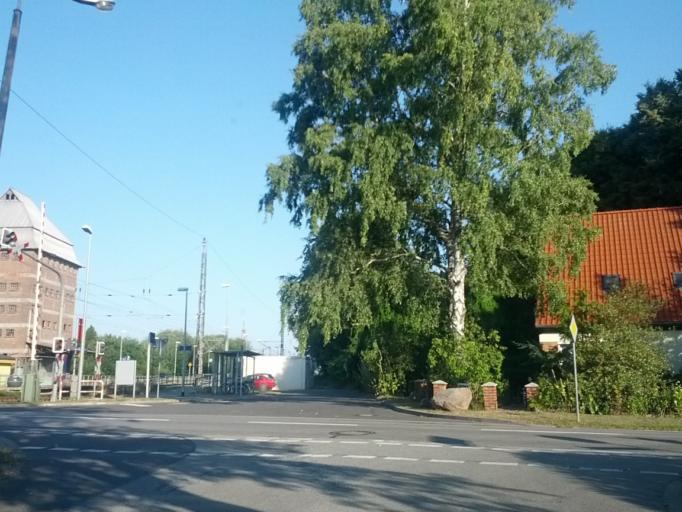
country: DE
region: Mecklenburg-Vorpommern
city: Brandshagen
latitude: 54.2007
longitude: 13.1986
